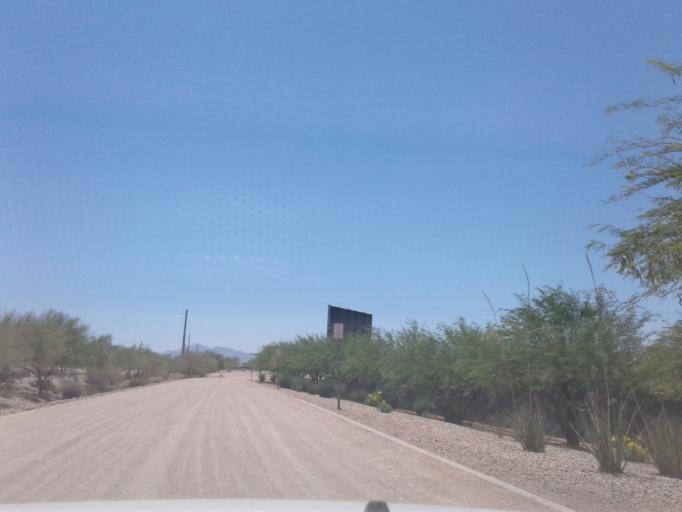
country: US
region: Arizona
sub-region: Maricopa County
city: Tolleson
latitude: 33.5108
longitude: -112.2904
